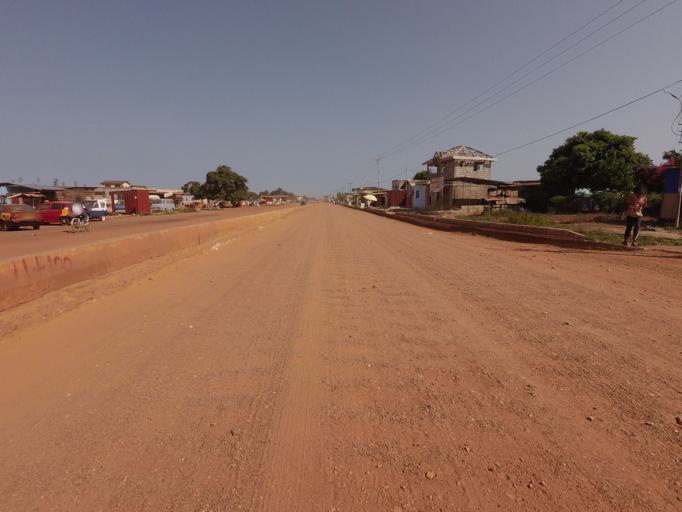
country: GH
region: Greater Accra
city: Teshi Old Town
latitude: 5.5859
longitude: -0.1145
